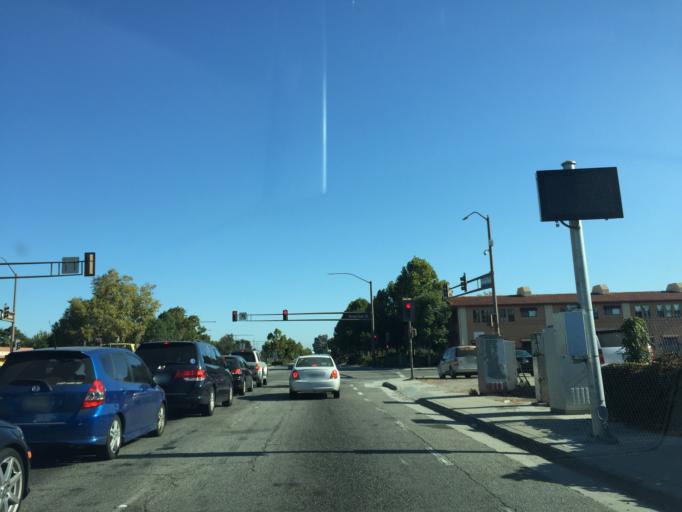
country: US
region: California
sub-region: San Mateo County
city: East Palo Alto
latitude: 37.4724
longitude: -122.1546
